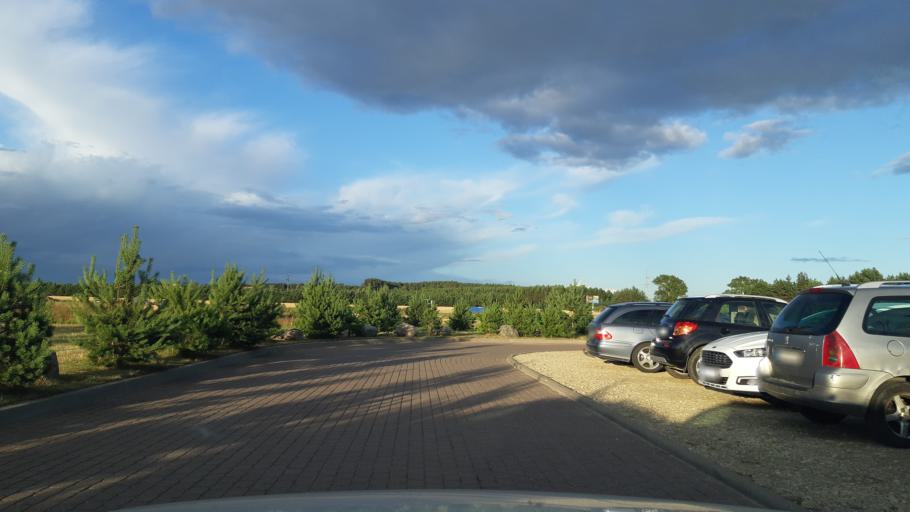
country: LT
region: Klaipedos apskritis
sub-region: Klaipeda
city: Palanga
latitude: 55.9586
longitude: 21.1280
